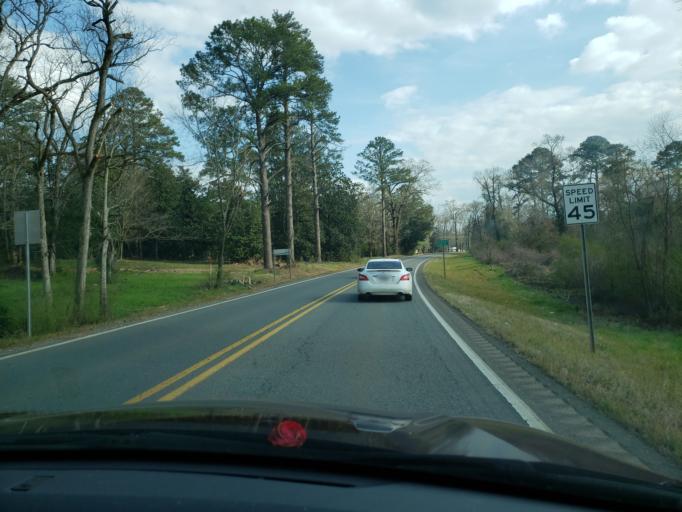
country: US
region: Alabama
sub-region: Hale County
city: Greensboro
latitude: 32.7074
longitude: -87.6081
